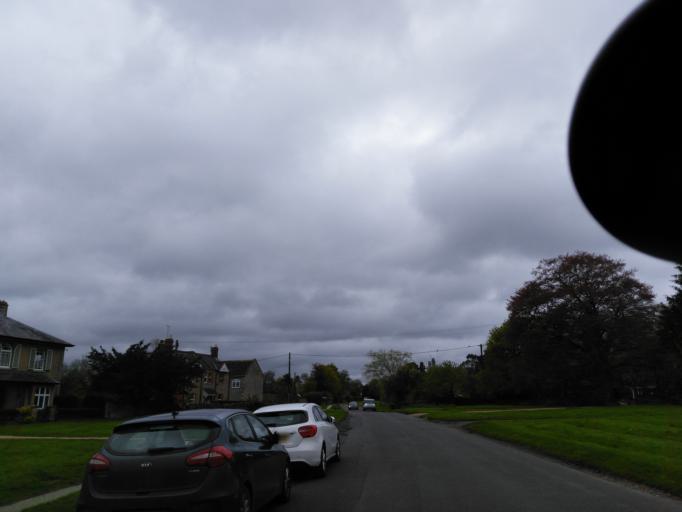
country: GB
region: England
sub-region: Wiltshire
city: Chippenham
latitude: 51.4907
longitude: -2.1133
